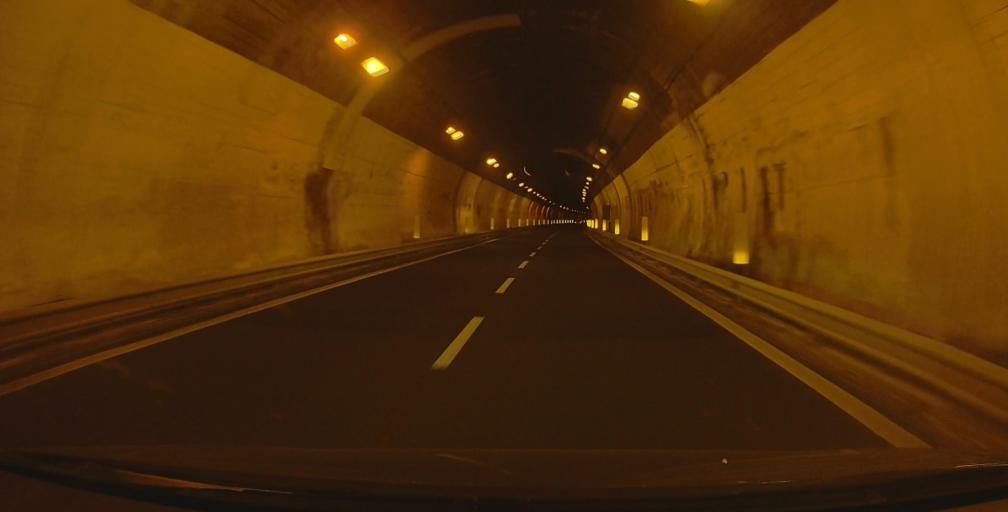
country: IT
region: Sicily
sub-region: Messina
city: Castelmola
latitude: 37.8516
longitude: 15.2775
